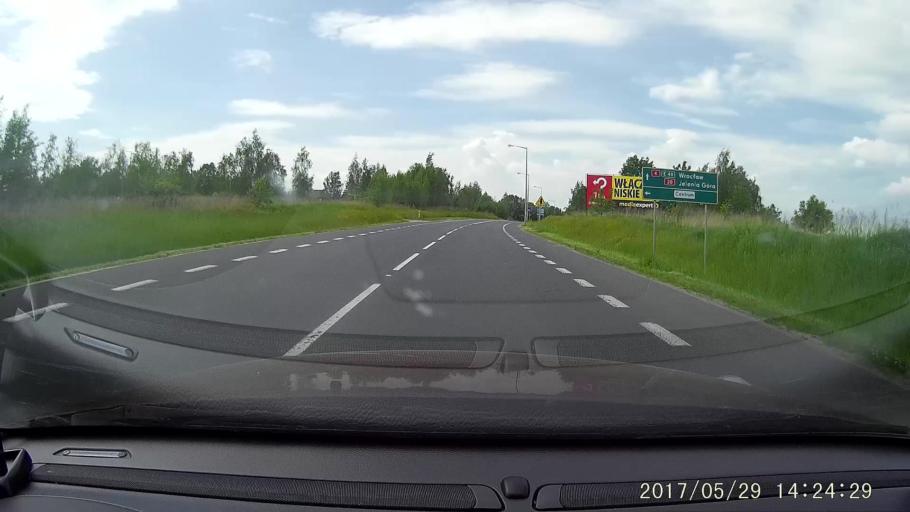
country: PL
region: Lower Silesian Voivodeship
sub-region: Powiat zgorzelecki
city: Lagow
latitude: 51.1483
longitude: 15.0306
